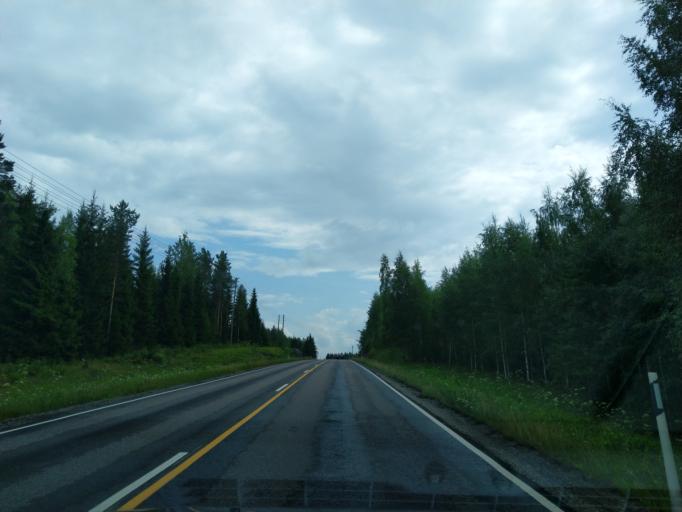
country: FI
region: South Karelia
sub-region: Imatra
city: Parikkala
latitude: 61.6192
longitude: 29.4432
